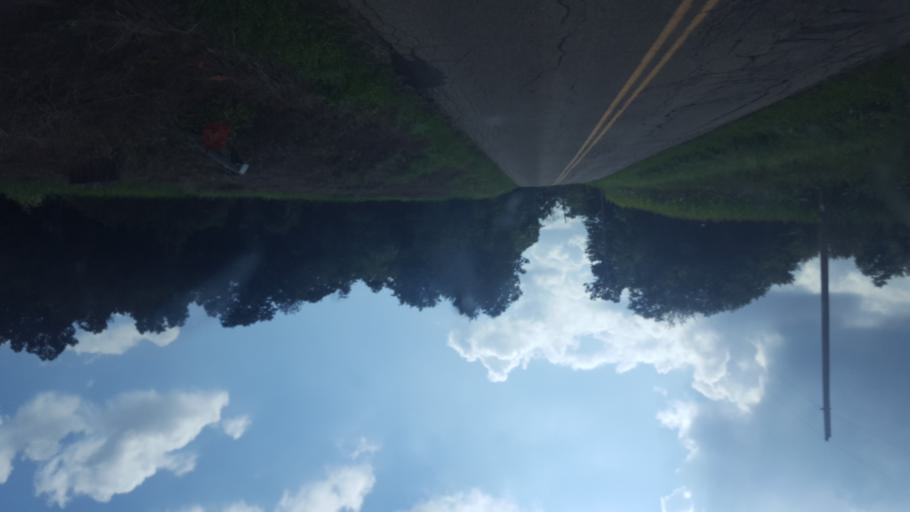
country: US
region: Ohio
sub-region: Knox County
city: Oak Hill
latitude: 40.4090
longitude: -82.2485
